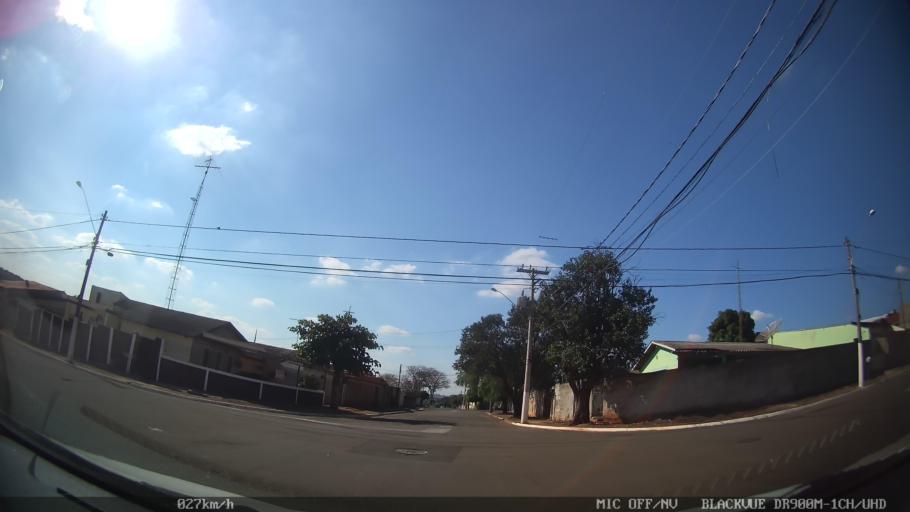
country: BR
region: Sao Paulo
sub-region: Sumare
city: Sumare
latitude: -22.8160
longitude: -47.2924
